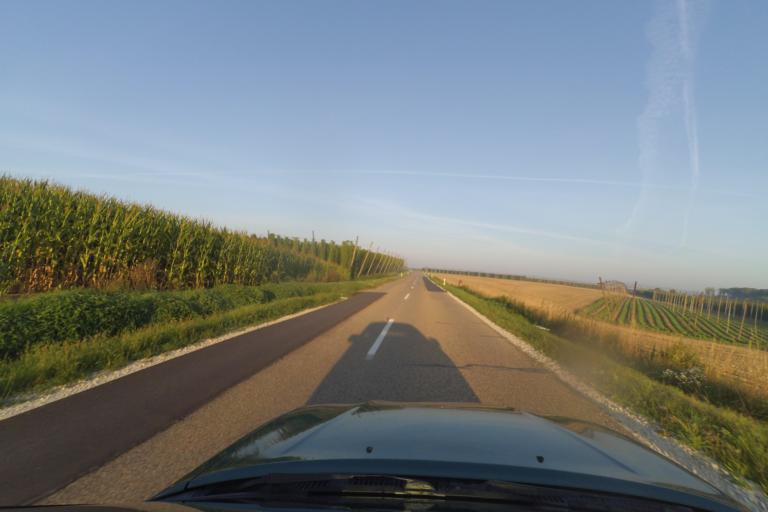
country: DE
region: Bavaria
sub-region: Upper Bavaria
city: Geisenfeld
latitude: 48.6805
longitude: 11.6570
